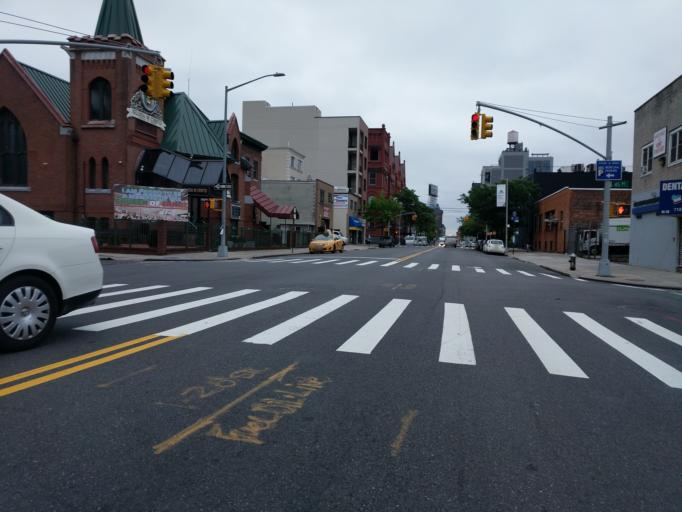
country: US
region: New York
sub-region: Queens County
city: Long Island City
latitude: 40.7468
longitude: -73.9478
